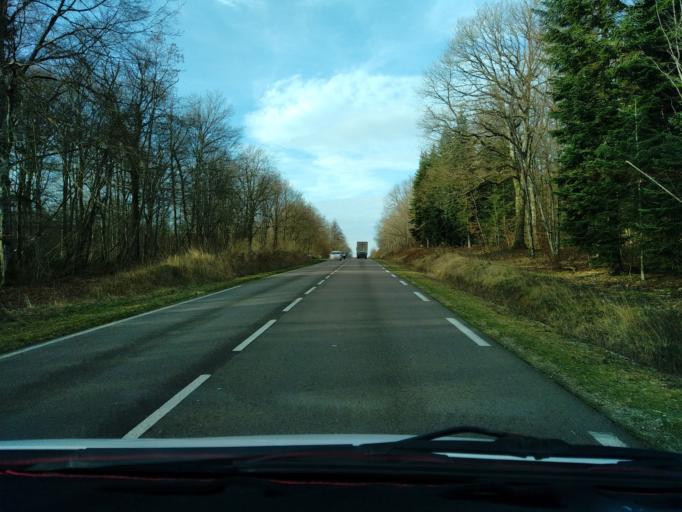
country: FR
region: Franche-Comte
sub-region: Departement de la Haute-Saone
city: Gray
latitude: 47.4077
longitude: 5.6349
